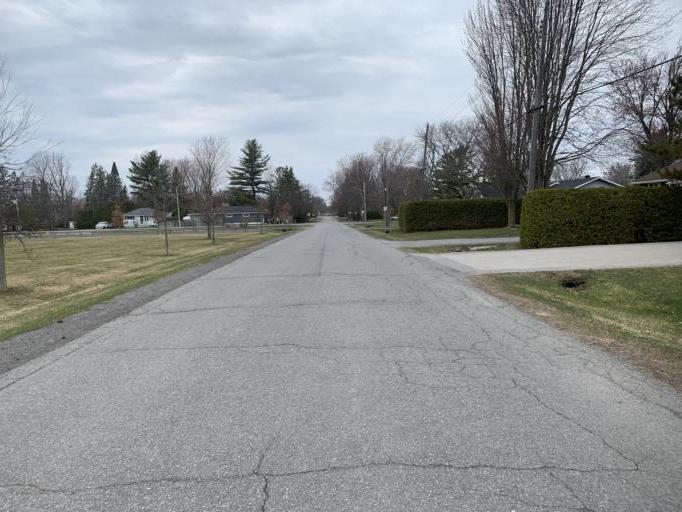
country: CA
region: Ontario
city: Bells Corners
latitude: 45.1883
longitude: -75.8262
